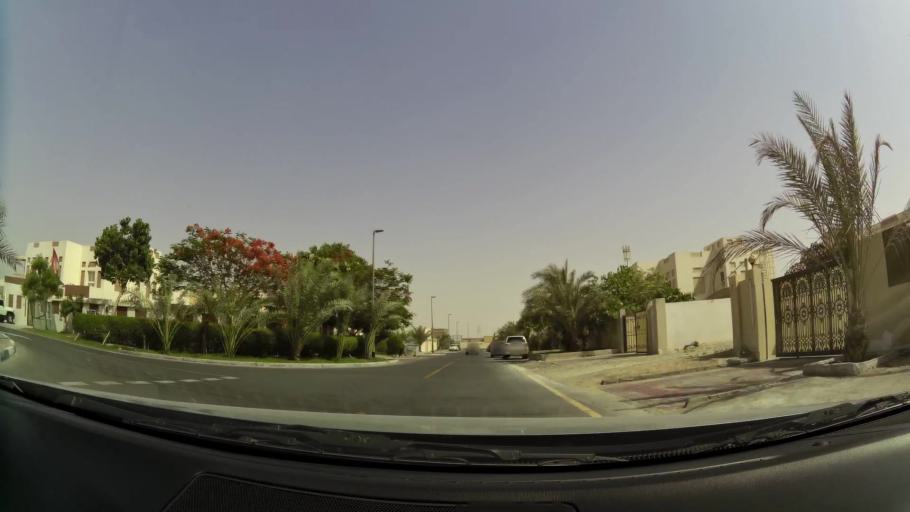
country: AE
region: Dubai
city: Dubai
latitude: 25.1503
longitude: 55.2547
